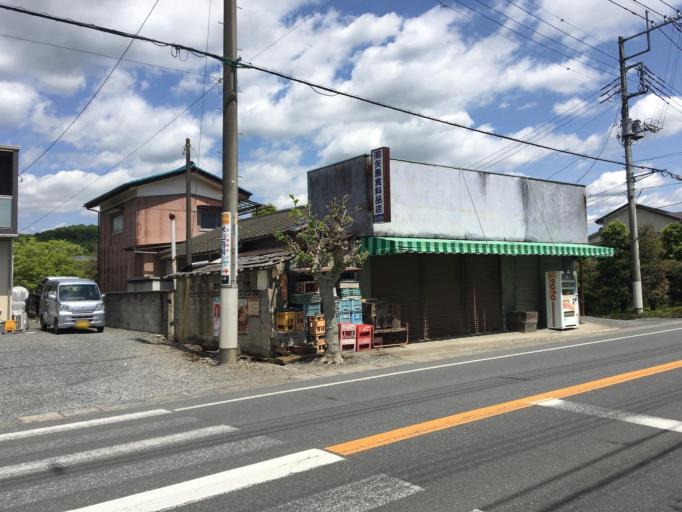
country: JP
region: Tochigi
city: Sano
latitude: 36.3260
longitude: 139.6101
